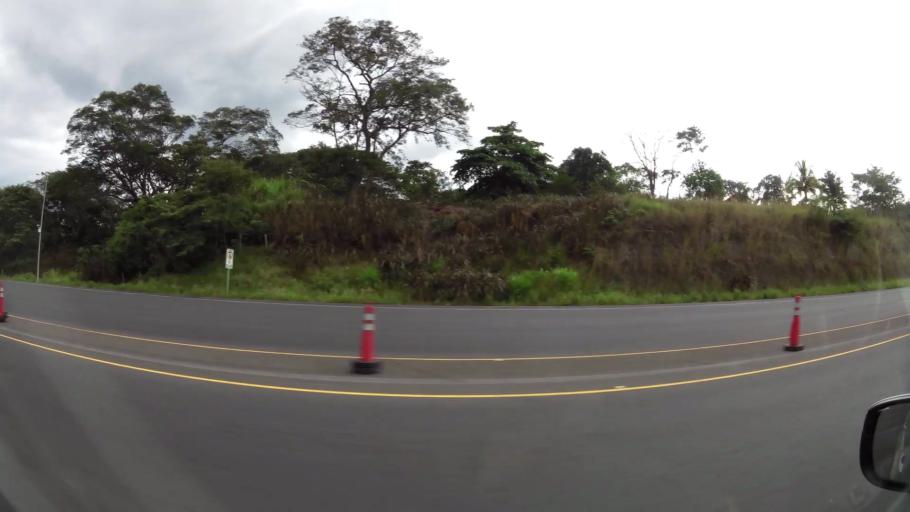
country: CR
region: Alajuela
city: Atenas
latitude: 9.9572
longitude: -84.3594
